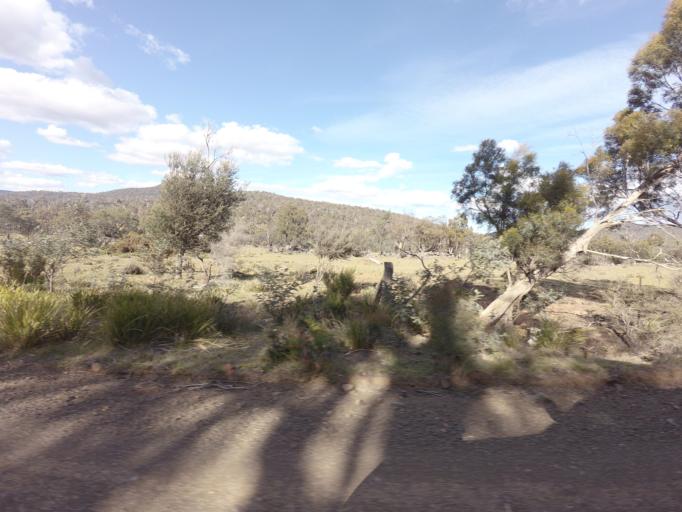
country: AU
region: Tasmania
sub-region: Break O'Day
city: St Helens
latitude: -41.8248
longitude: 148.0095
